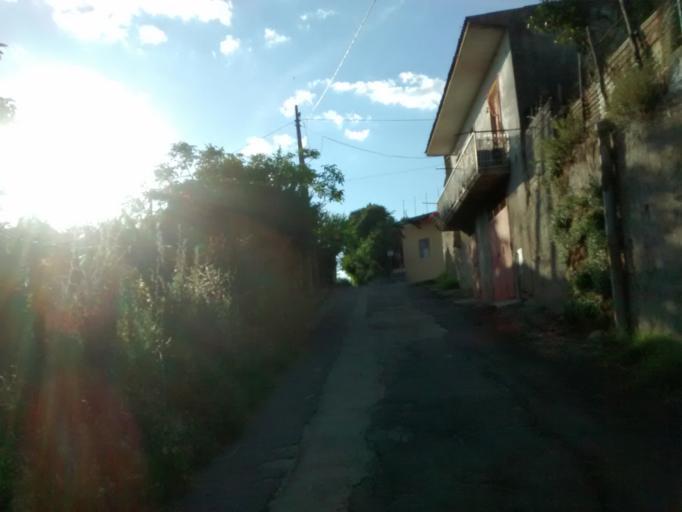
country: IT
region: Calabria
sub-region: Provincia di Catanzaro
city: Cortale
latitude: 38.8875
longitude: 16.4067
